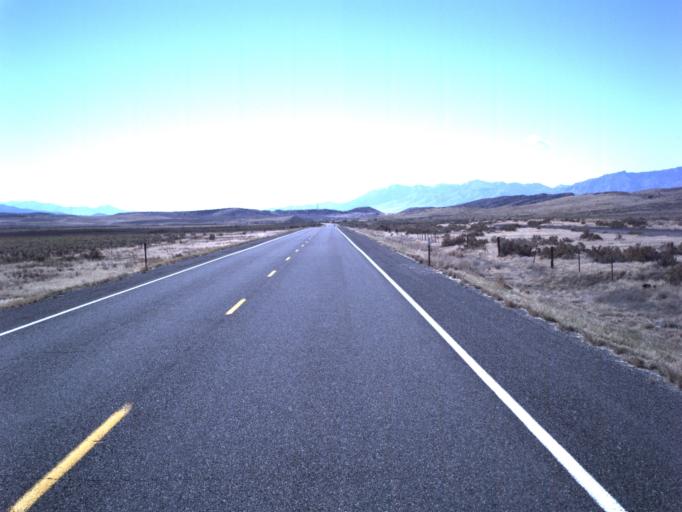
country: US
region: Utah
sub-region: Juab County
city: Nephi
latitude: 39.5062
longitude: -111.9523
